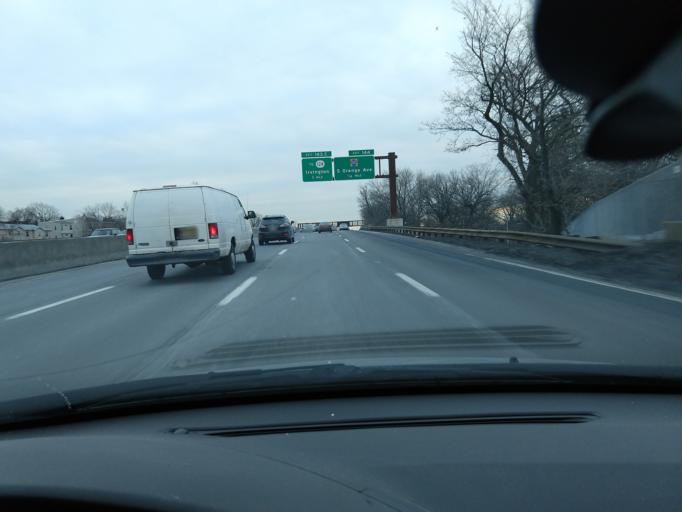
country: US
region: New Jersey
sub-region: Essex County
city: East Orange
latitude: 40.7457
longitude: -74.2135
